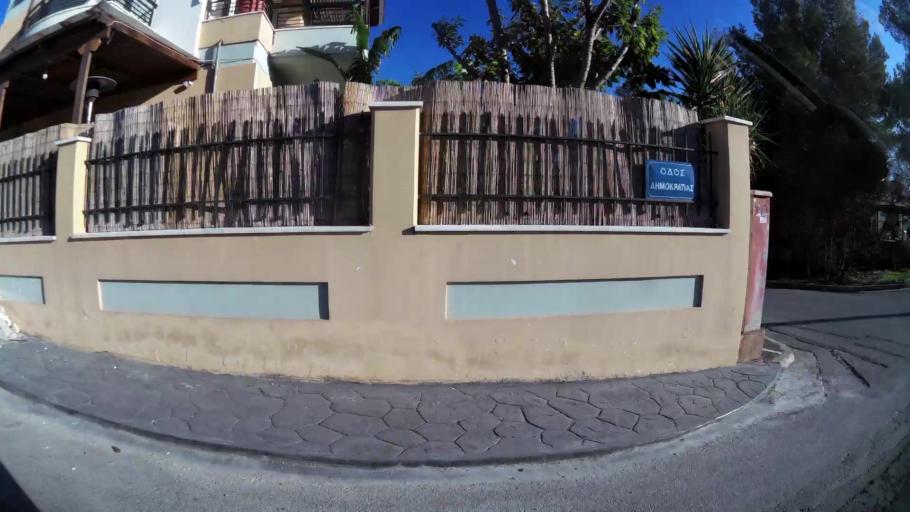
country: GR
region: Attica
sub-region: Nomarchia Anatolikis Attikis
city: Rafina
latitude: 38.0286
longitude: 23.9990
